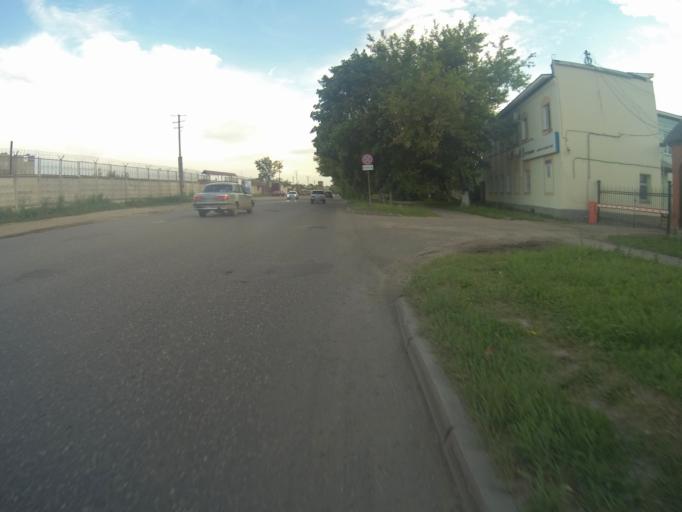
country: RU
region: Vladimir
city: Vladimir
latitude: 56.1578
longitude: 40.3845
